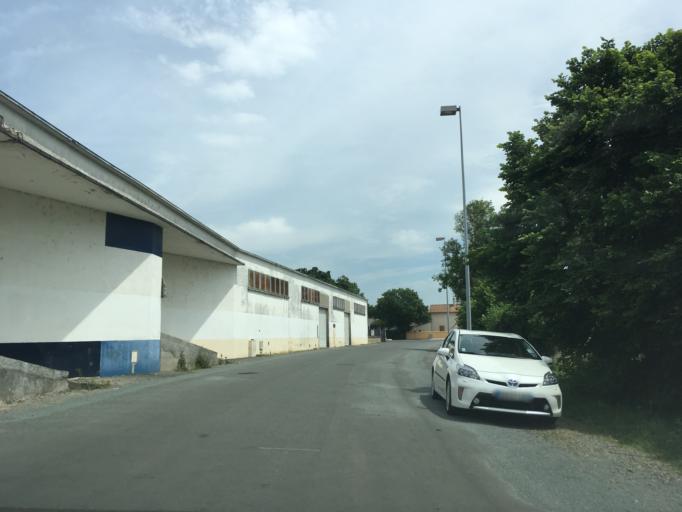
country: FR
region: Poitou-Charentes
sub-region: Departement des Deux-Sevres
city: Niort
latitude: 46.3075
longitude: -0.4621
